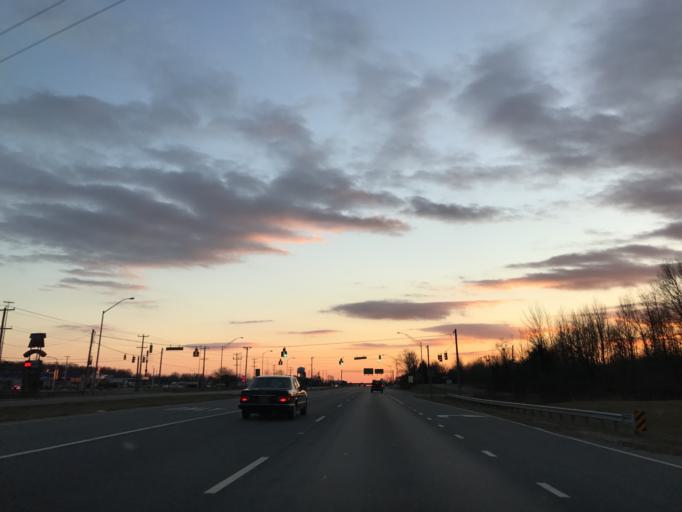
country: US
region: Maryland
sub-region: Cecil County
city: Elkton
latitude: 39.6467
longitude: -75.7967
